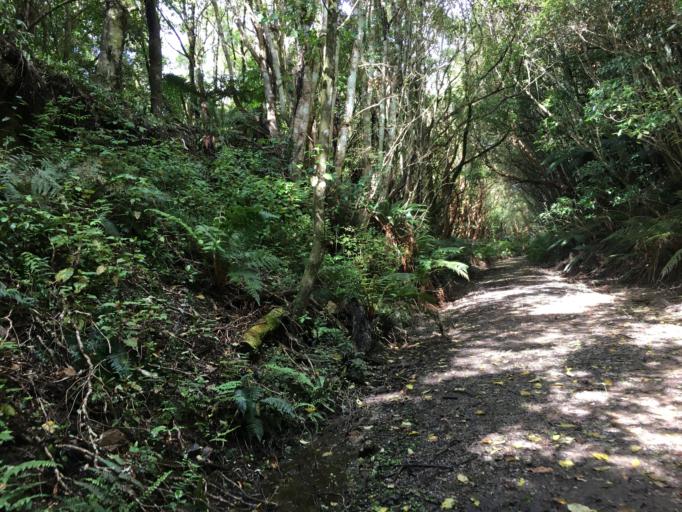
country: NZ
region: Otago
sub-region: Clutha District
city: Papatowai
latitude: -46.4963
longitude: 169.4799
